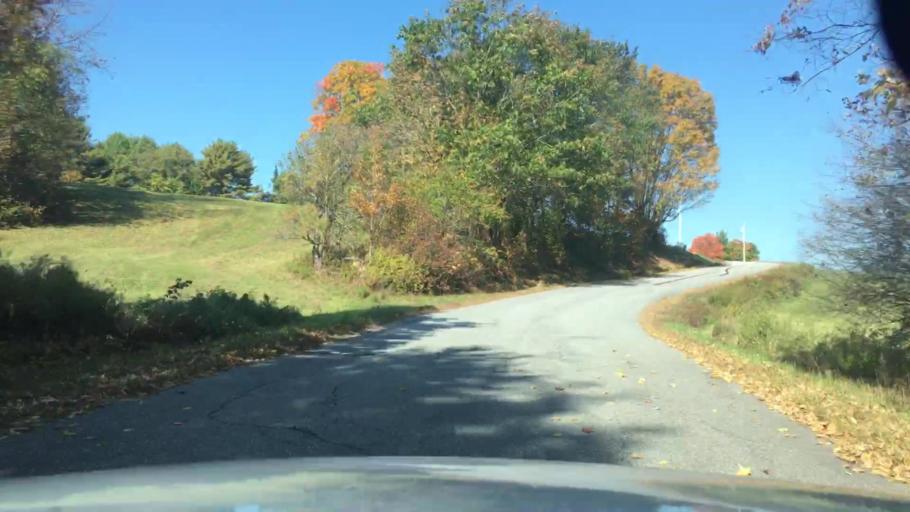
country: US
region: Maine
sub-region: Sagadahoc County
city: Topsham
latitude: 44.0095
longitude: -69.9616
